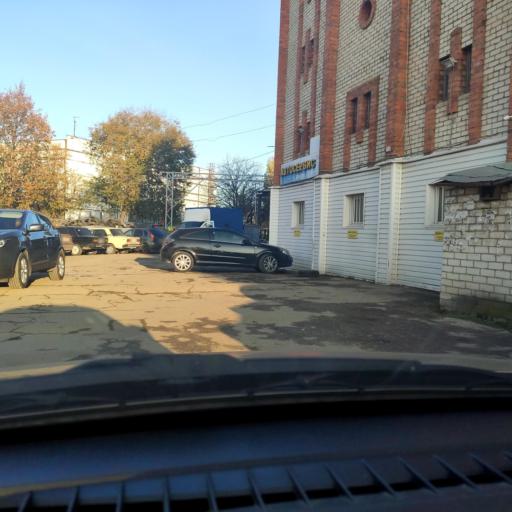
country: RU
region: Samara
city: Tol'yatti
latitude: 53.5424
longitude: 49.3134
